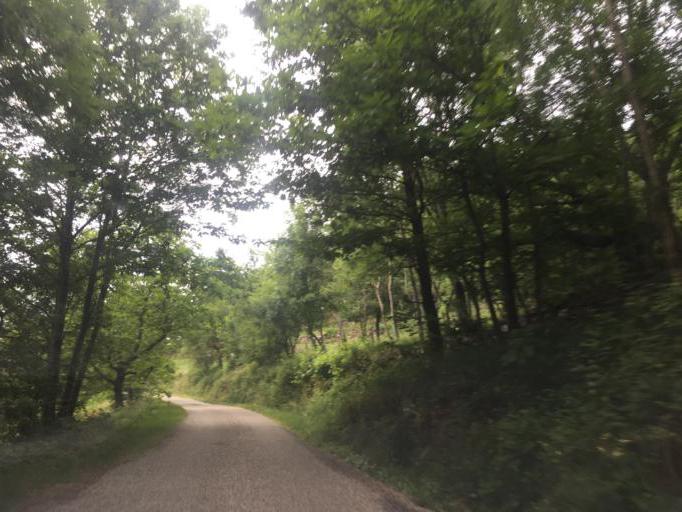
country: FR
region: Rhone-Alpes
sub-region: Departement de l'Ardeche
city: Flaviac
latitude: 44.7861
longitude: 4.6383
